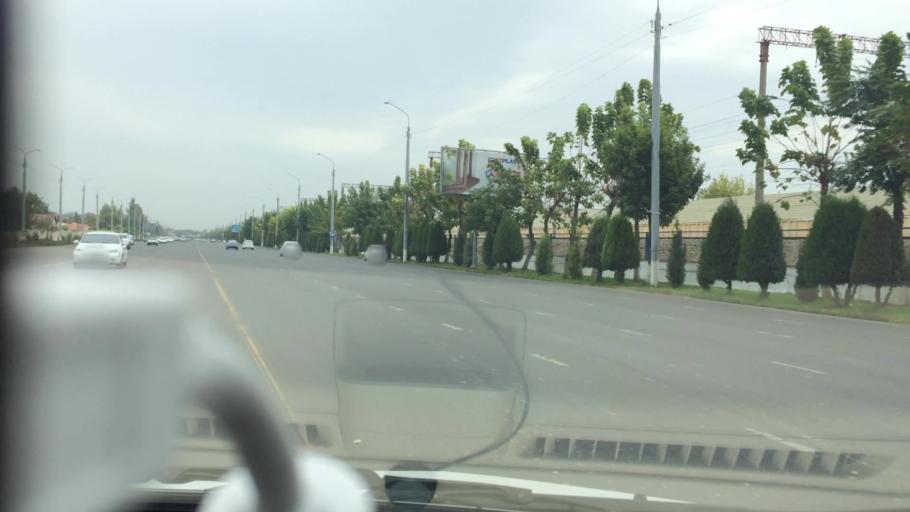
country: UZ
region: Toshkent Shahri
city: Tashkent
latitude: 41.2782
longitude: 69.2728
